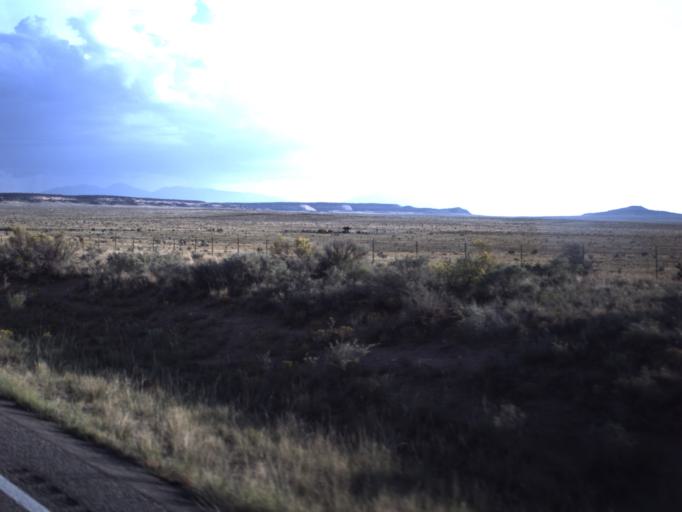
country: US
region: Utah
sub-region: San Juan County
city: Monticello
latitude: 38.1736
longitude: -109.3797
